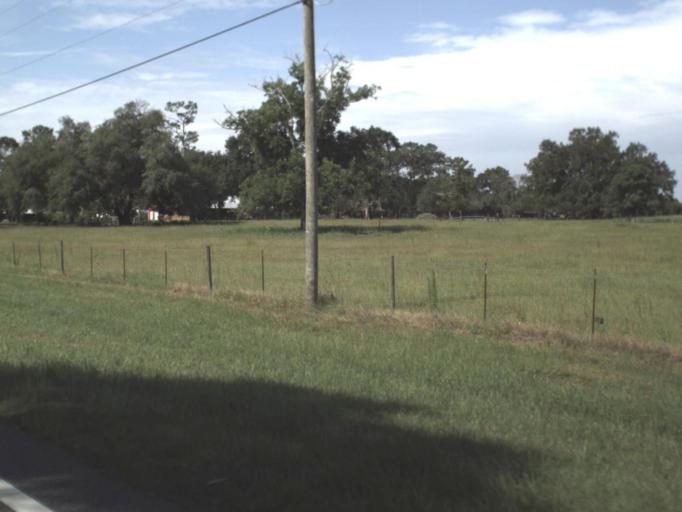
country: US
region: Florida
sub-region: Madison County
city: Madison
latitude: 30.5439
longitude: -83.3675
